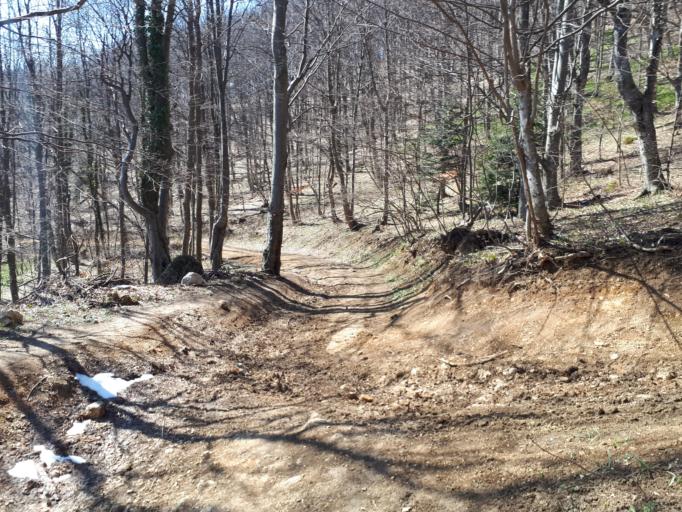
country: HR
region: Varazdinska
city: Ivanec
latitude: 46.1781
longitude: 16.1360
